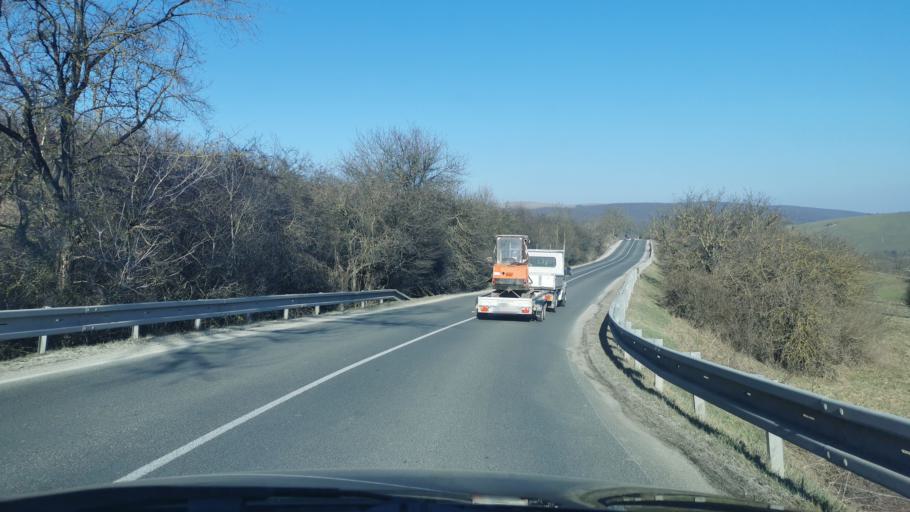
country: SK
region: Trnavsky
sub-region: Okres Senica
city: Senica
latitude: 48.7352
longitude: 17.4271
